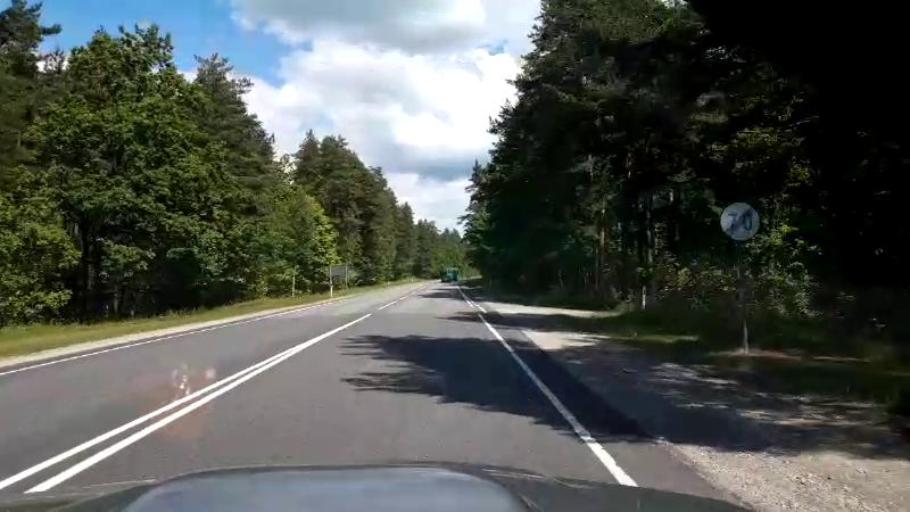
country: EE
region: Paernumaa
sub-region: Paikuse vald
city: Paikuse
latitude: 58.2858
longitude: 24.5806
